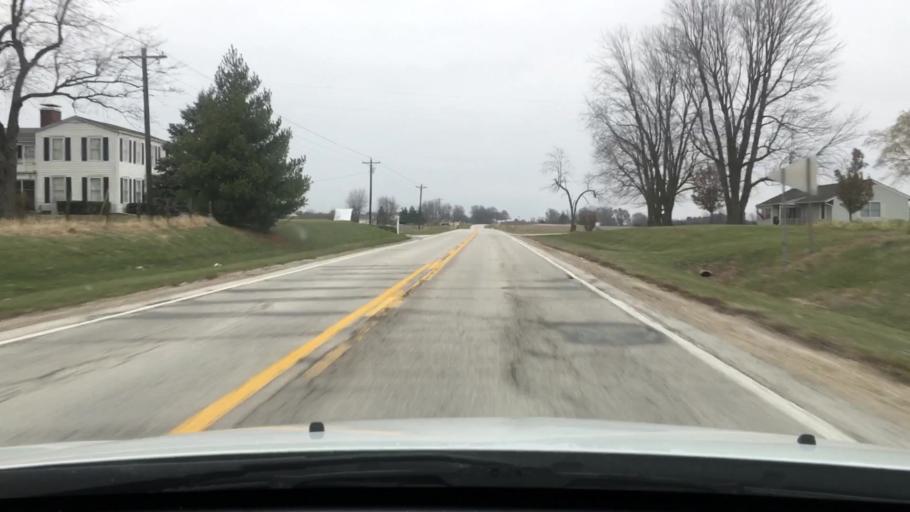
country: US
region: Illinois
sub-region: Pike County
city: Pittsfield
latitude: 39.5565
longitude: -90.9165
